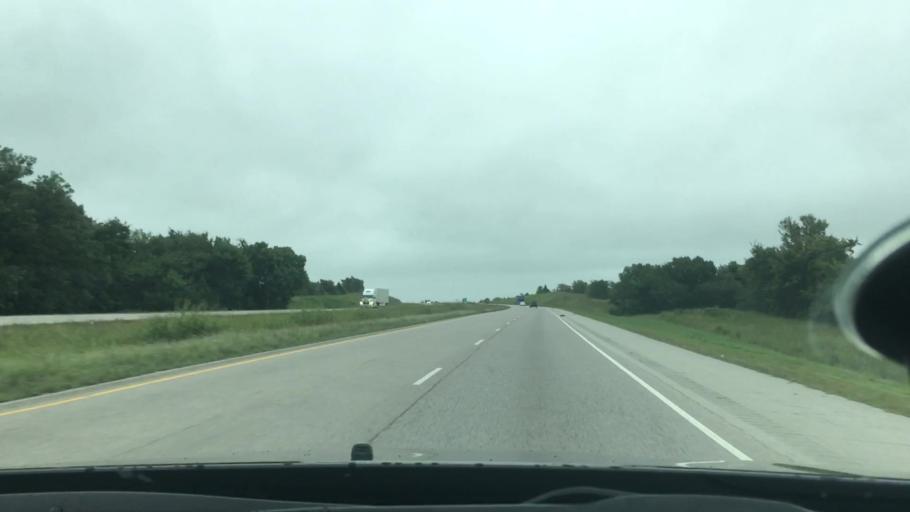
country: US
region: Oklahoma
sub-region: Okfuskee County
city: Okemah
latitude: 35.4159
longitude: -96.3277
